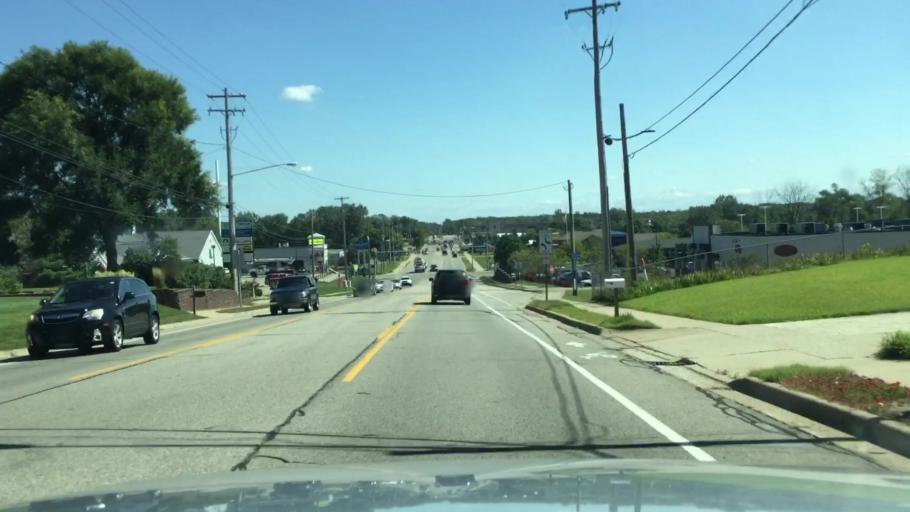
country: US
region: Michigan
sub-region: Kalamazoo County
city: Portage
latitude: 42.2155
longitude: -85.5974
